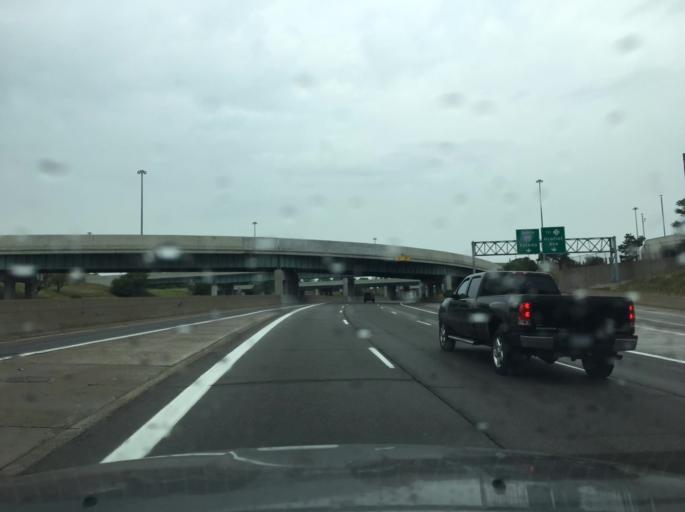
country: US
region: Michigan
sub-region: Wayne County
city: Detroit
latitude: 42.3415
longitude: -83.0429
